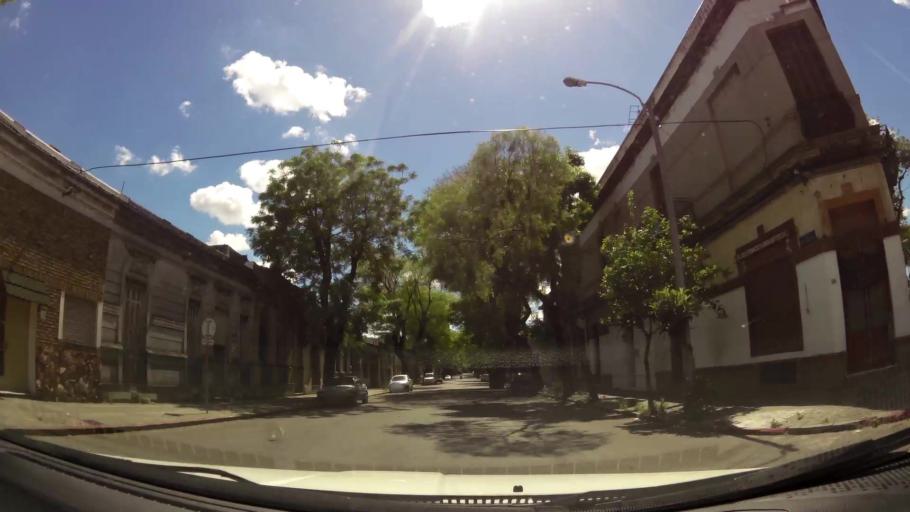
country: UY
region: Montevideo
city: Montevideo
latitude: -34.8837
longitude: -56.1907
